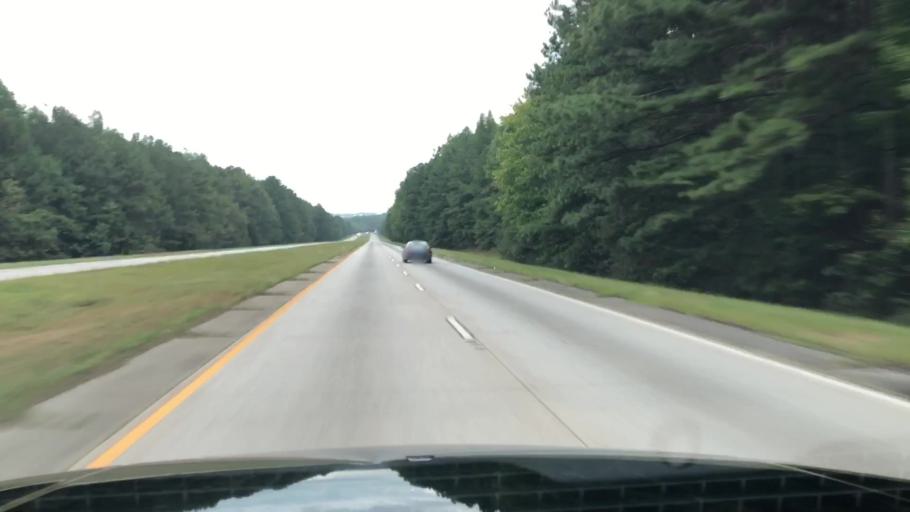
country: US
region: Georgia
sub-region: Cobb County
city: Mableton
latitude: 33.7044
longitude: -84.5767
